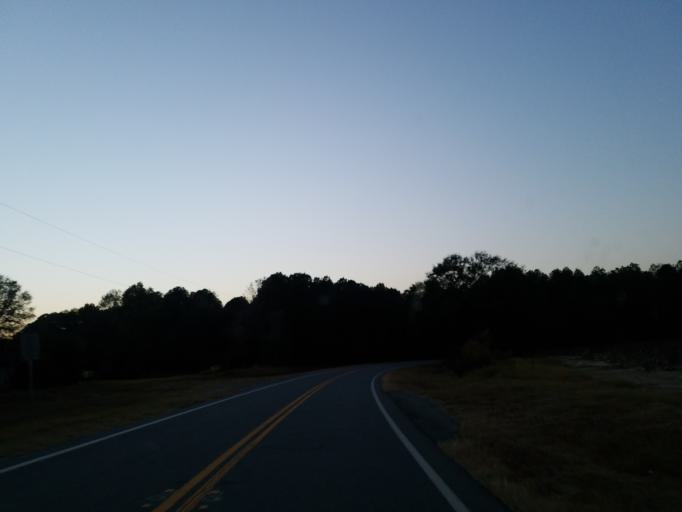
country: US
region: Georgia
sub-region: Wilcox County
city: Rochelle
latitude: 31.8104
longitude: -83.4948
